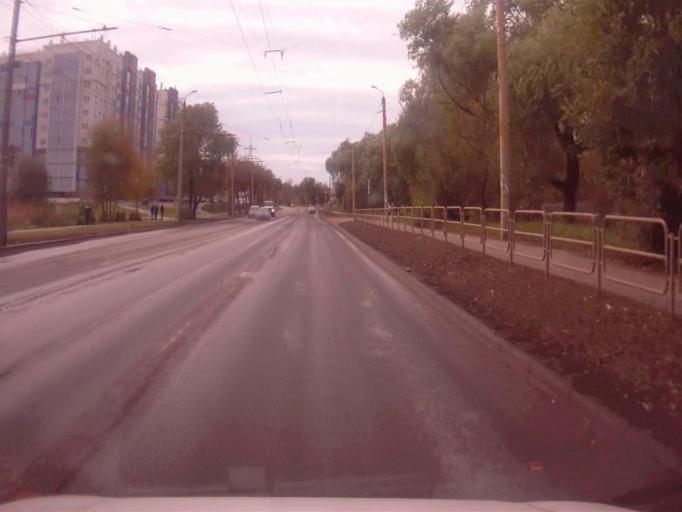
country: RU
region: Chelyabinsk
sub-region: Gorod Chelyabinsk
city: Chelyabinsk
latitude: 55.1163
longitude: 61.4318
